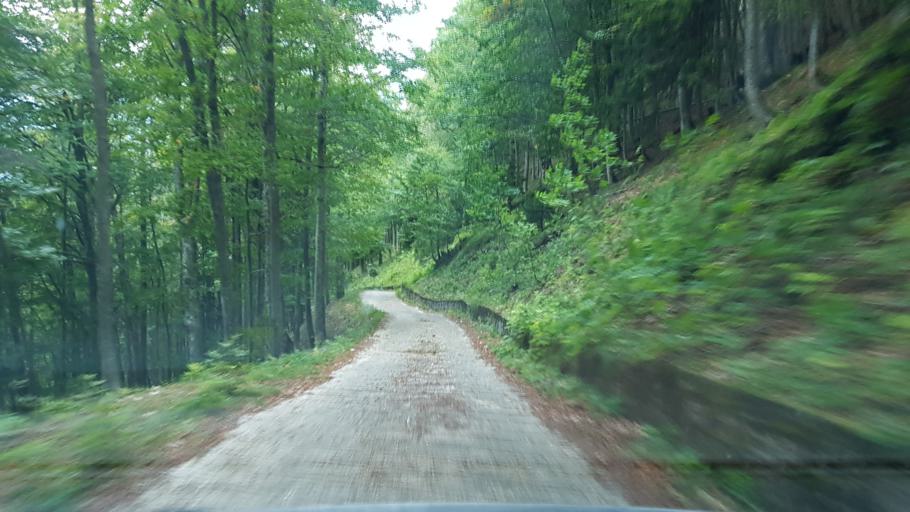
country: SI
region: Bovec
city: Bovec
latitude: 46.4112
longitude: 13.5092
